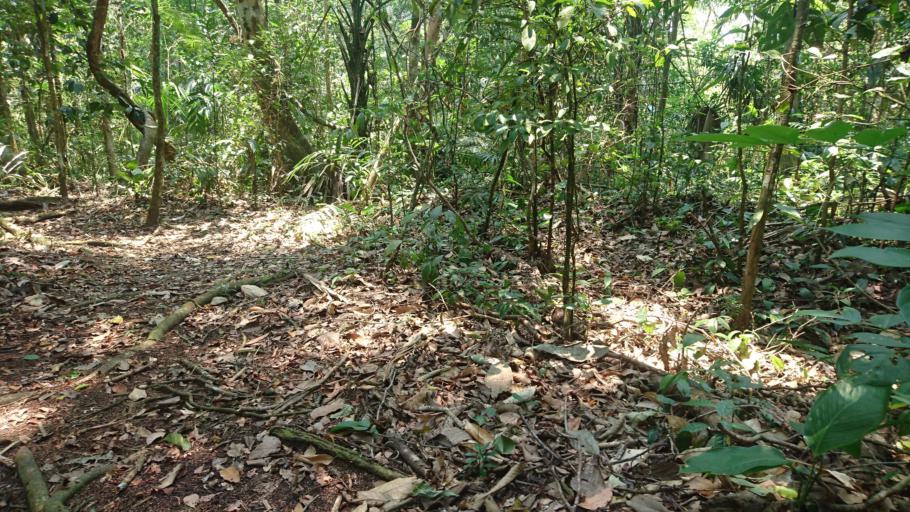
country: MX
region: Chiapas
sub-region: Marques de Comillas
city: Zamora Pico de Oro
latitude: 16.2479
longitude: -90.8319
